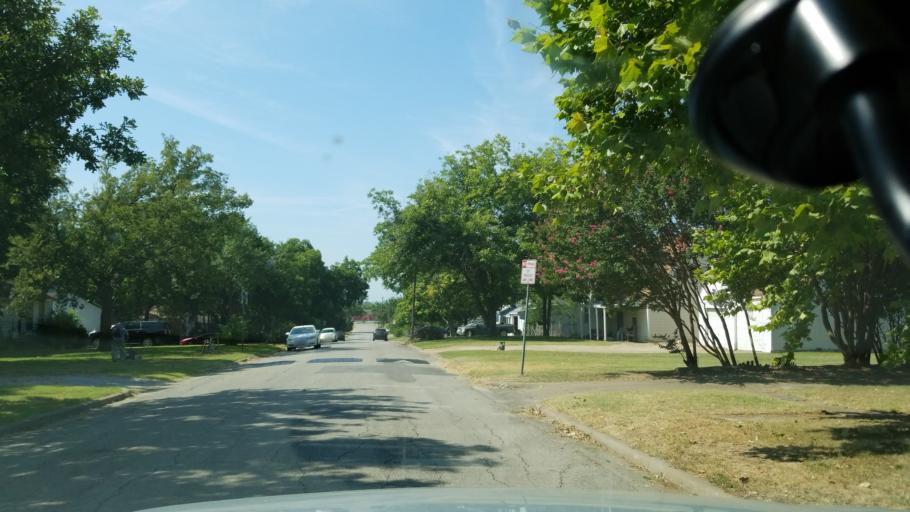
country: US
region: Texas
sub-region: Dallas County
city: Grand Prairie
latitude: 32.7522
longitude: -96.9587
